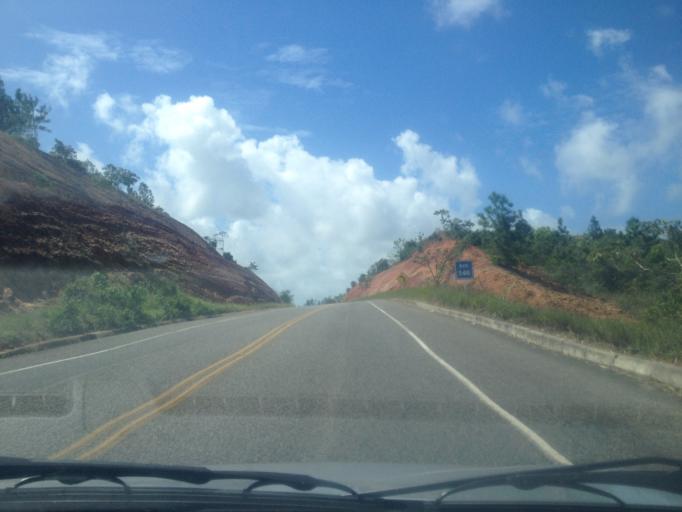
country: BR
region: Bahia
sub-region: Conde
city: Conde
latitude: -11.8804
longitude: -37.6477
